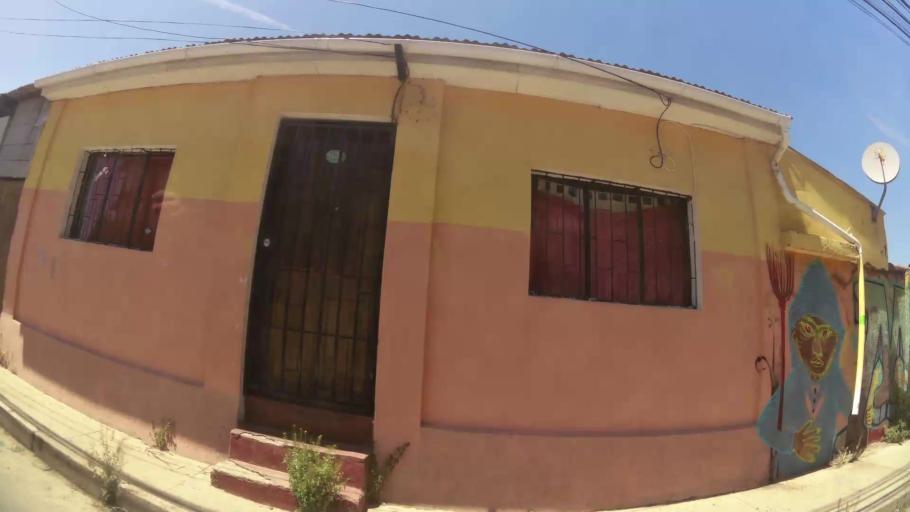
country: CL
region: Valparaiso
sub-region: Provincia de Valparaiso
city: Valparaiso
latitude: -33.0371
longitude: -71.6368
